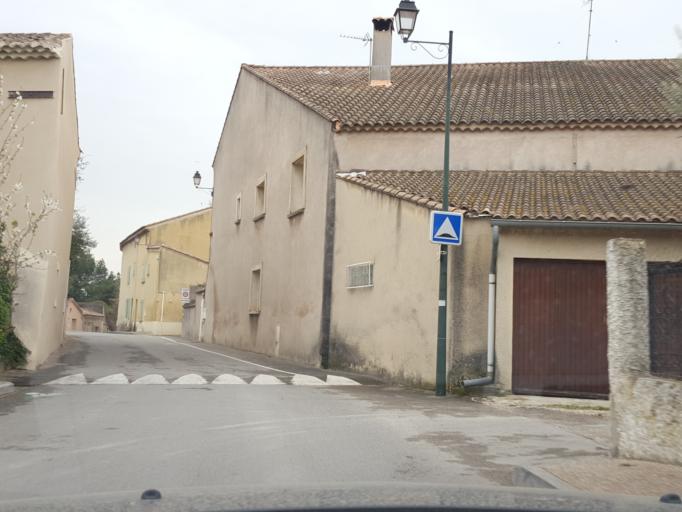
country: FR
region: Provence-Alpes-Cote d'Azur
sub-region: Departement du Vaucluse
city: Saint-Saturnin-les-Avignon
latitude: 43.9593
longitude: 4.9290
